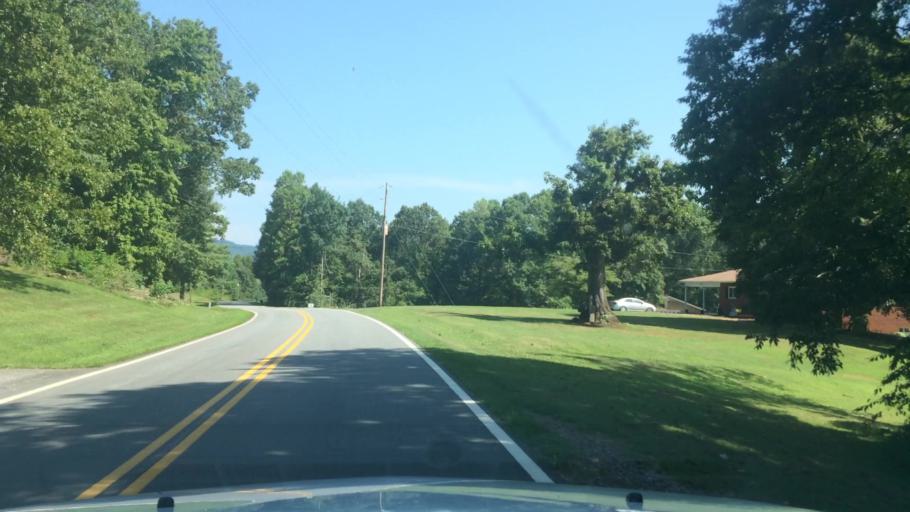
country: US
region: North Carolina
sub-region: Alexander County
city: Taylorsville
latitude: 35.9512
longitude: -81.2672
